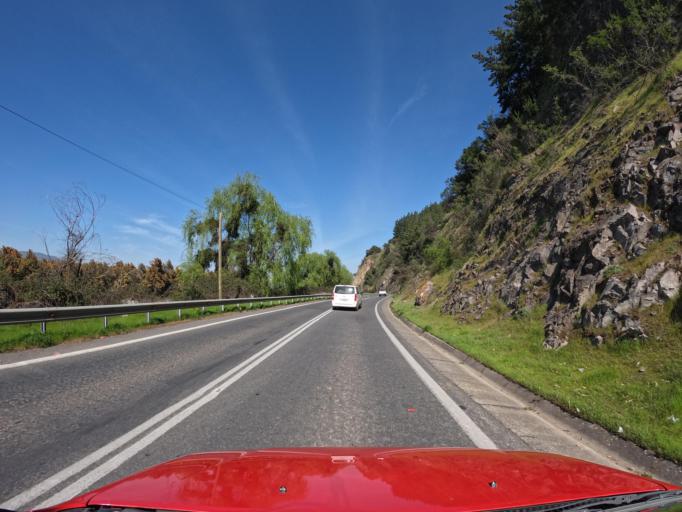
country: CL
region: Maule
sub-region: Provincia de Curico
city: Rauco
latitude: -34.9858
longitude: -71.4251
